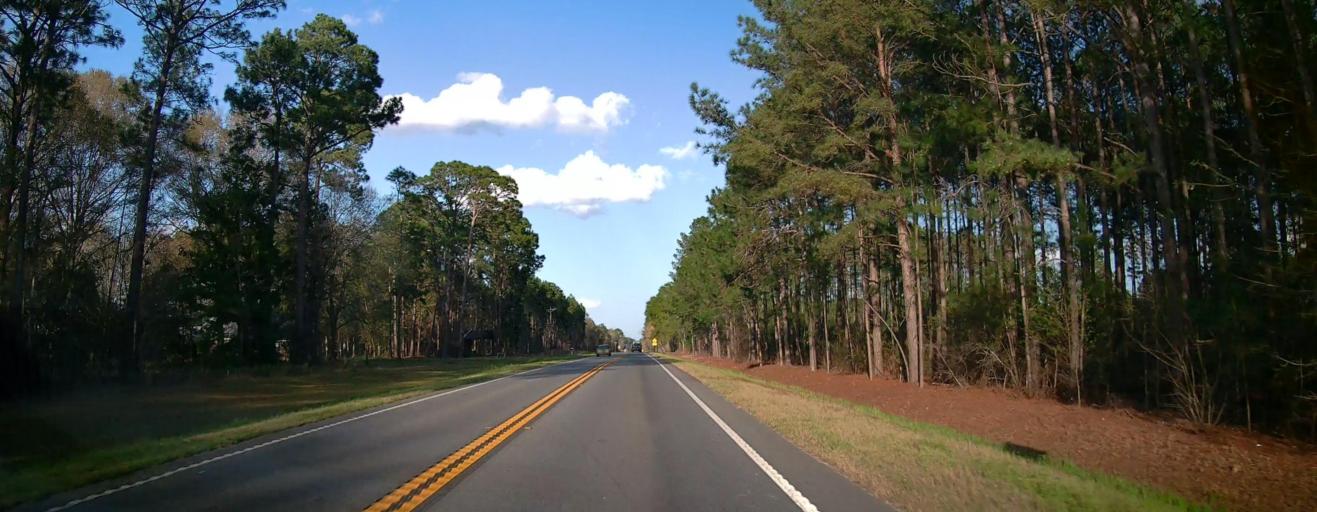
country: US
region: Georgia
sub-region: Tattnall County
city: Reidsville
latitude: 32.1218
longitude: -82.0656
